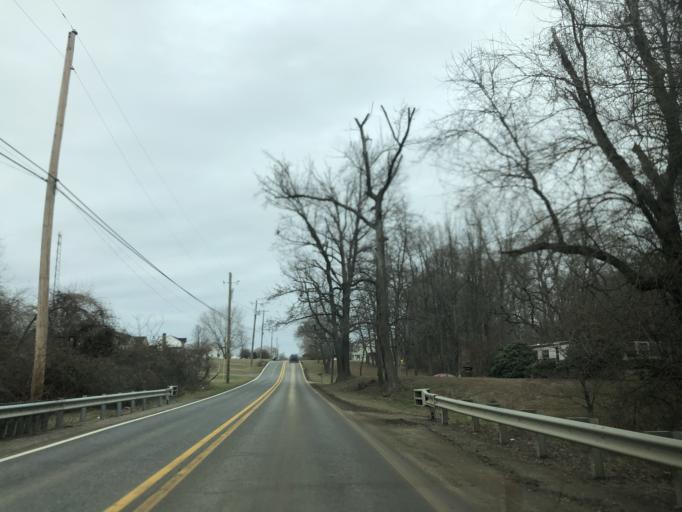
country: US
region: Delaware
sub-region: New Castle County
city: Middletown
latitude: 39.4845
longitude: -75.6964
